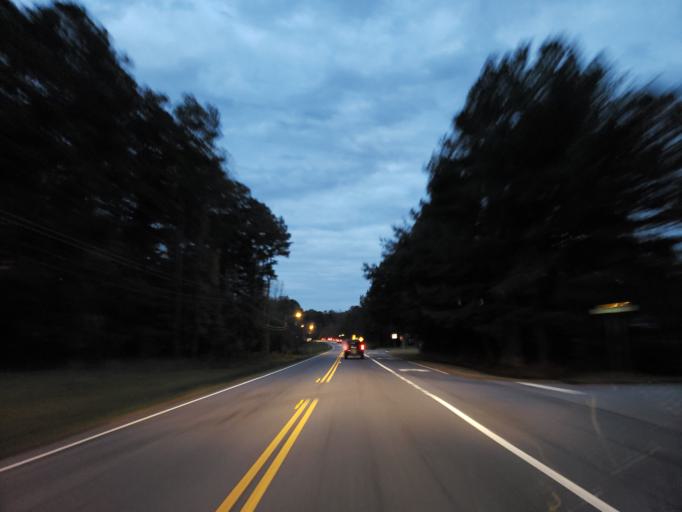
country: US
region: Georgia
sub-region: Cobb County
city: Powder Springs
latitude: 33.9201
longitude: -84.6931
